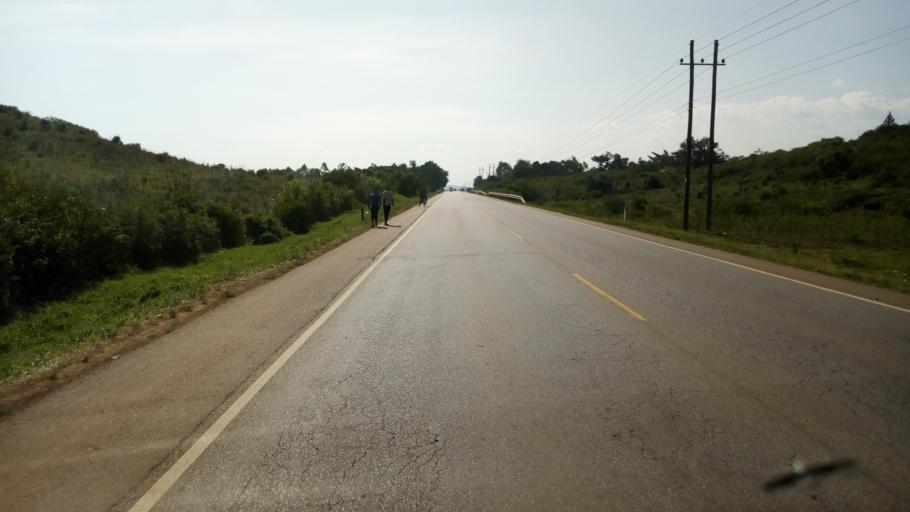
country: UG
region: Eastern Region
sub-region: Busia District
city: Busia
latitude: 0.5300
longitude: 33.9391
